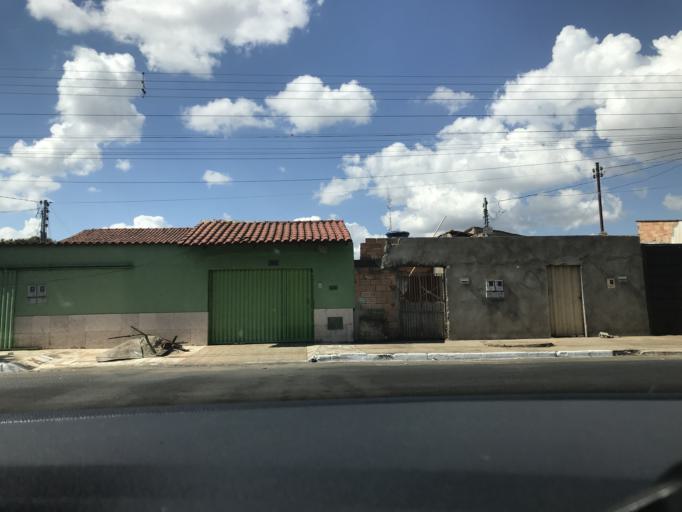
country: BR
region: Goias
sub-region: Senador Canedo
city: Senador Canedo
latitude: -16.6514
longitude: -49.1530
